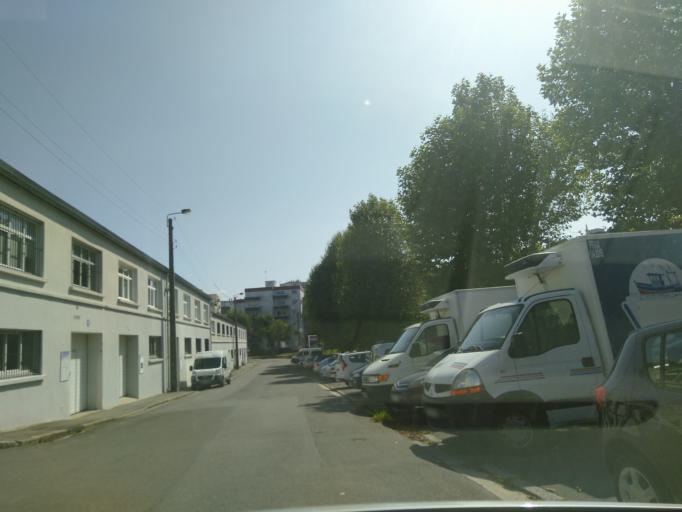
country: FR
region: Brittany
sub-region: Departement du Finistere
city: Brest
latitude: 48.3963
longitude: -4.4677
